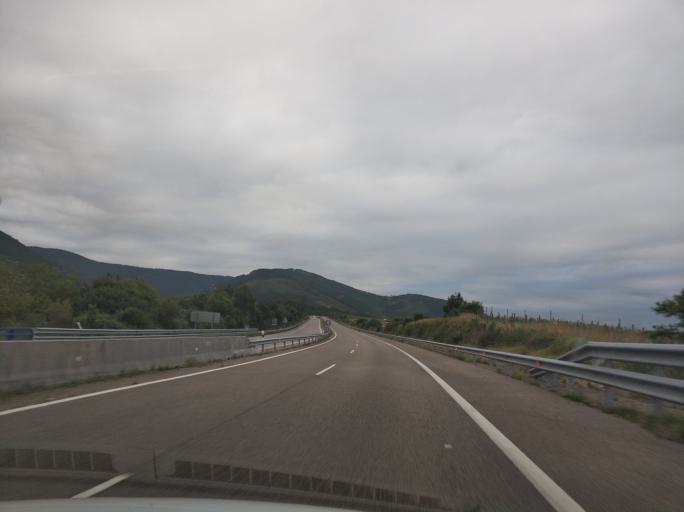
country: ES
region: Asturias
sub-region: Province of Asturias
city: Tineo
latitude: 43.5468
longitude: -6.4696
